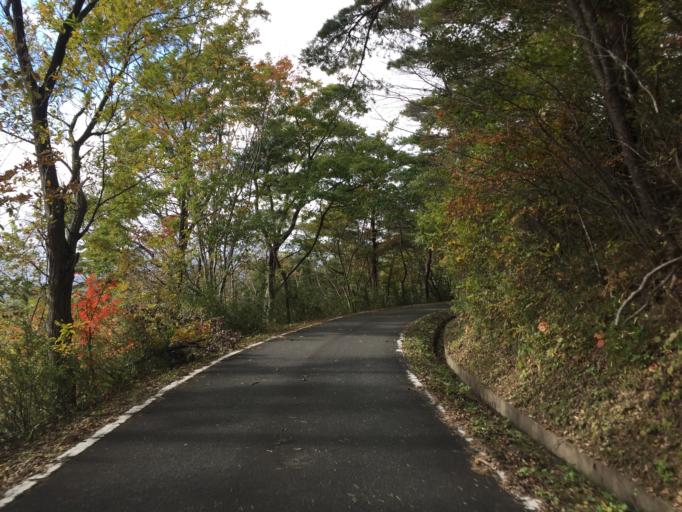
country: JP
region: Fukushima
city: Nihommatsu
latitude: 37.6766
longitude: 140.3758
